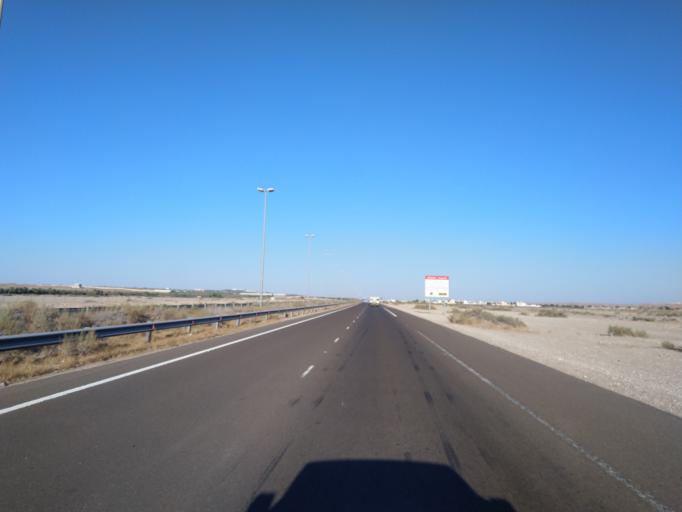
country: OM
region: Al Buraimi
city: Al Buraymi
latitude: 24.5043
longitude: 55.4572
